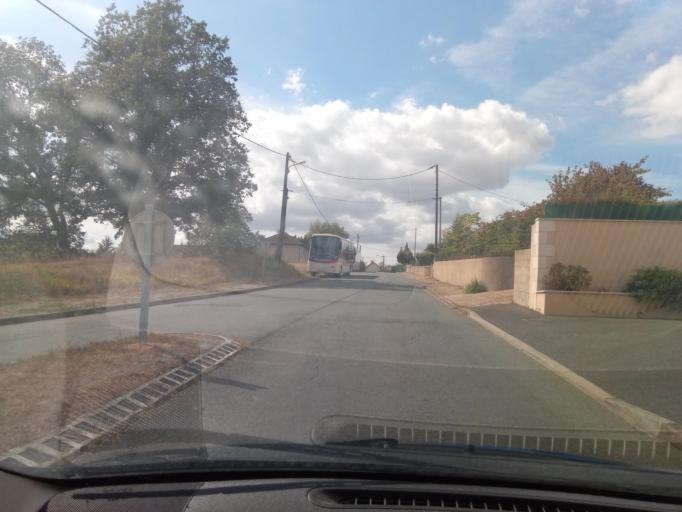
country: FR
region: Poitou-Charentes
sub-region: Departement de la Vienne
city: Saint-Savin
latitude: 46.5610
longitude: 0.8629
